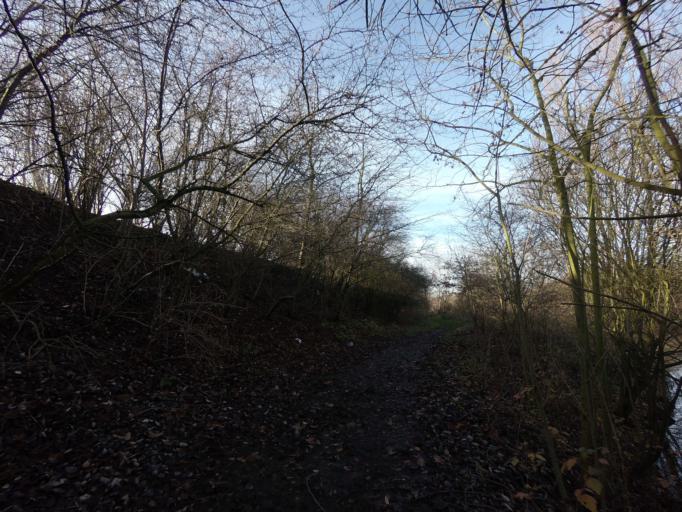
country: BE
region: Flanders
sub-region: Provincie Antwerpen
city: Kapellen
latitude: 51.2766
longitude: 4.3977
